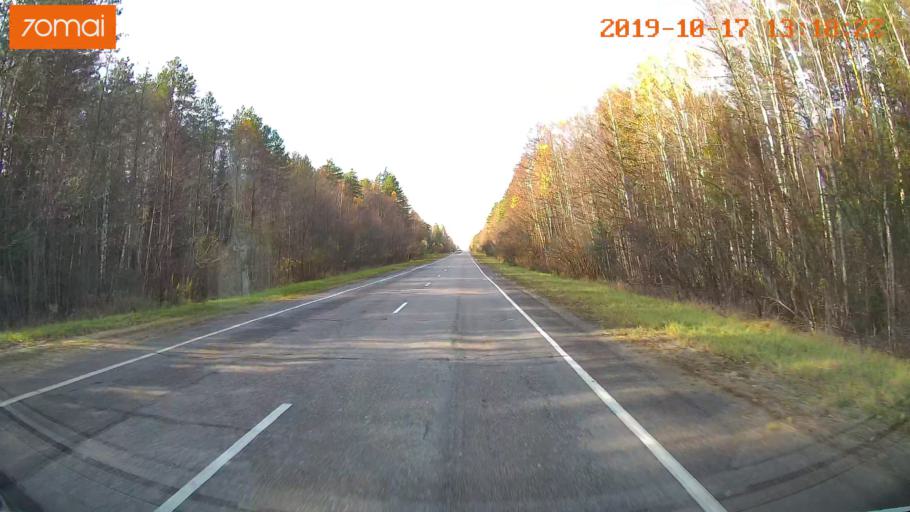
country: RU
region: Rjazan
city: Gus'-Zheleznyy
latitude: 55.0625
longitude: 41.0993
